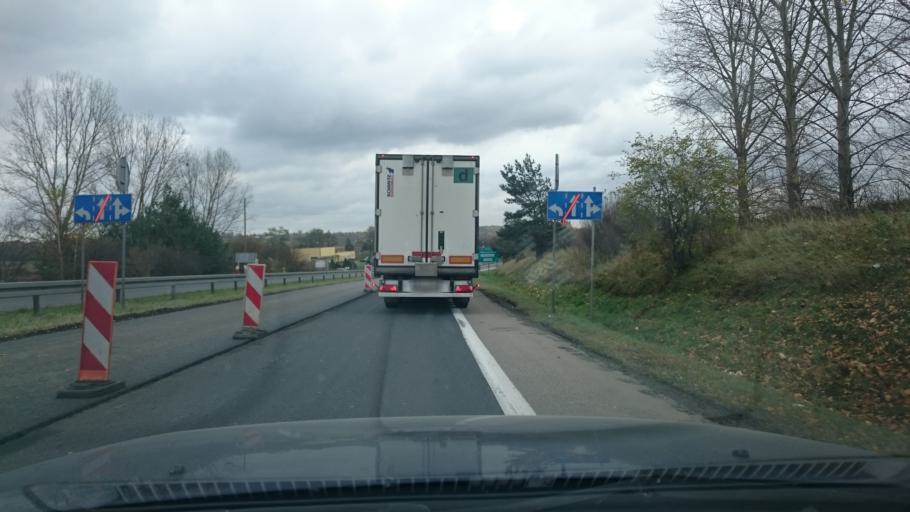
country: PL
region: Silesian Voivodeship
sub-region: Powiat bedzinski
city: Slawkow
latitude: 50.3044
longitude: 19.3854
